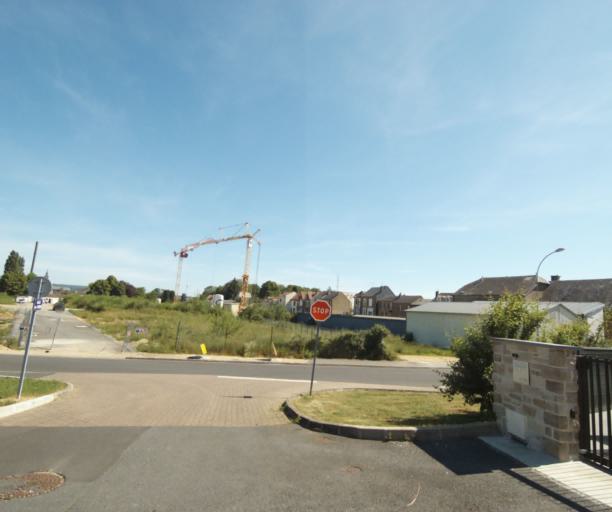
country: FR
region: Champagne-Ardenne
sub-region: Departement des Ardennes
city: Charleville-Mezieres
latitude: 49.7520
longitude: 4.7146
